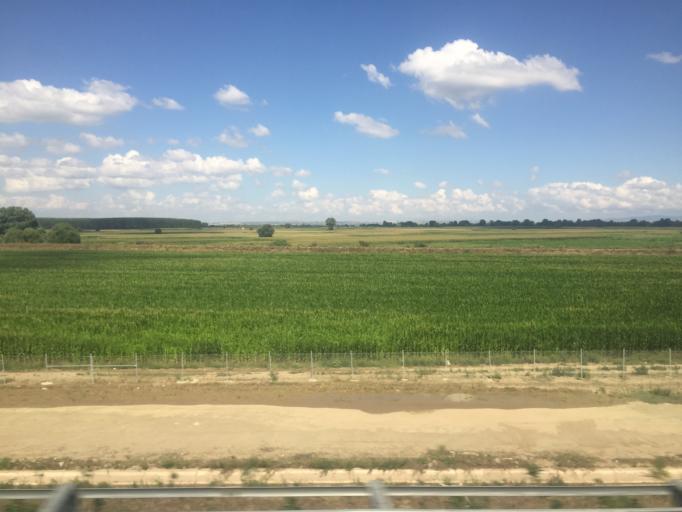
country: TR
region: Bursa
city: Tatkavakli
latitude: 40.0925
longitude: 28.2748
